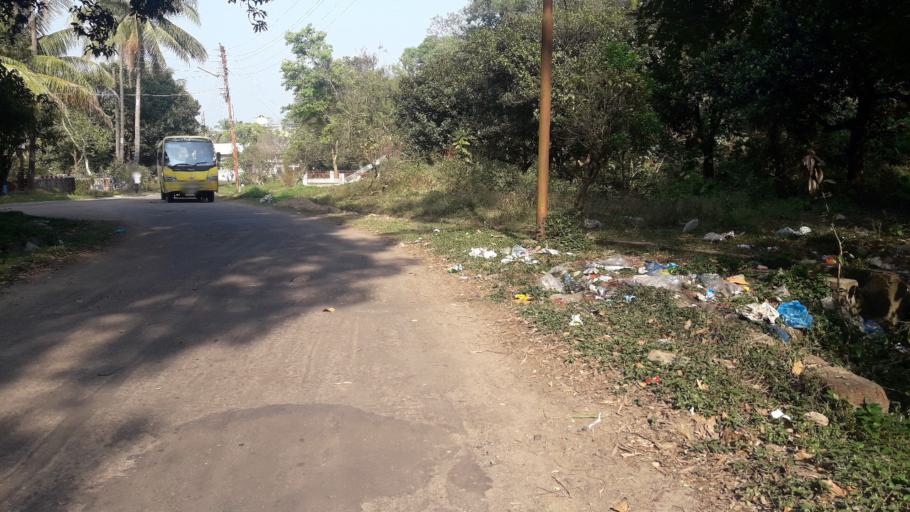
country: BD
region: Chittagong
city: Chittagong
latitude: 22.4667
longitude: 91.7925
